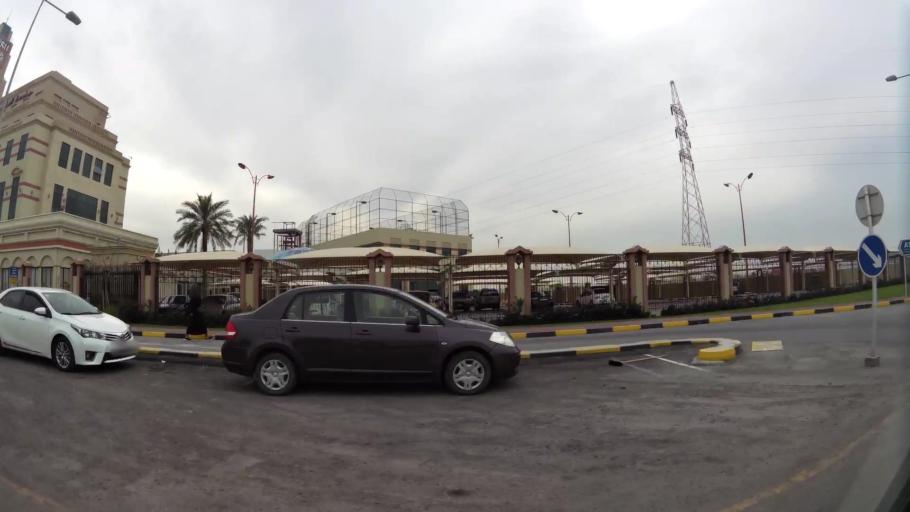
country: BH
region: Northern
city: Sitrah
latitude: 26.1440
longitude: 50.6153
